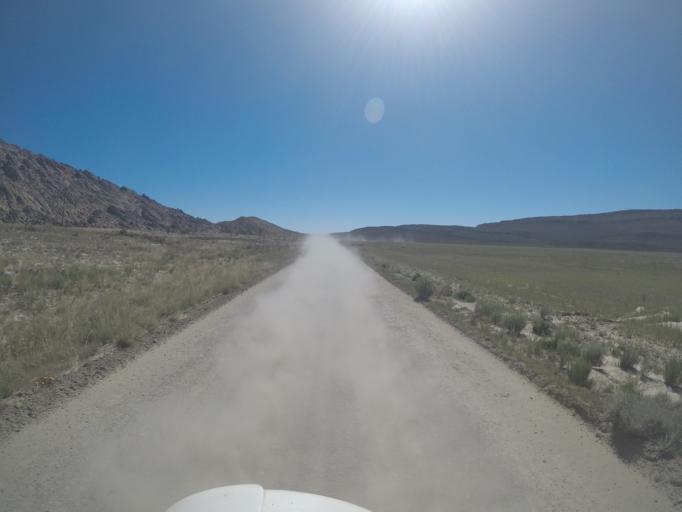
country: ZA
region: Western Cape
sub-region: Cape Winelands District Municipality
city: Ceres
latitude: -32.8357
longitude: 19.4507
